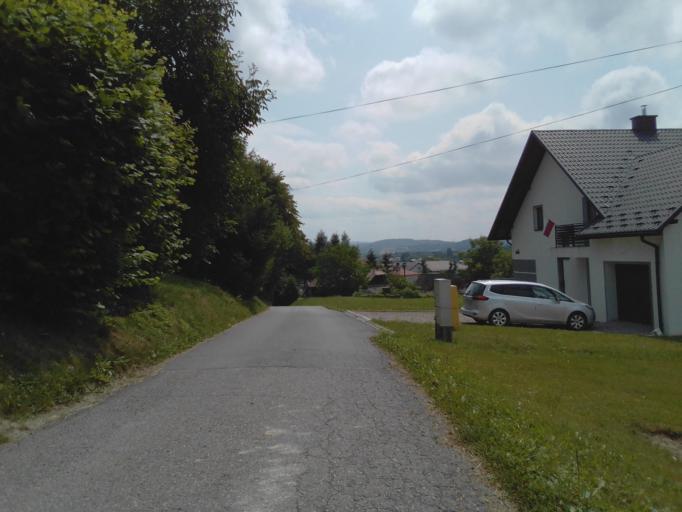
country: PL
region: Subcarpathian Voivodeship
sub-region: Powiat strzyzowski
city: Czudec
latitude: 49.9465
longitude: 21.8334
